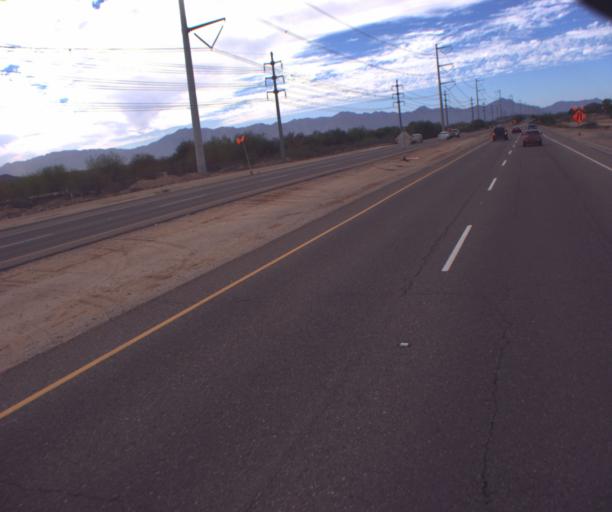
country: US
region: Arizona
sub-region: Maricopa County
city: Guadalupe
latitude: 33.2915
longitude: -112.0021
